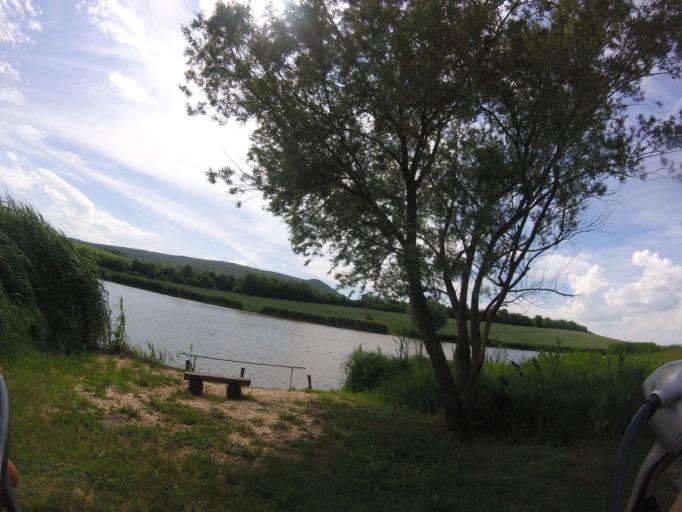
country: HU
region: Komarom-Esztergom
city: Tarjan
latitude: 47.5808
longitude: 18.5592
